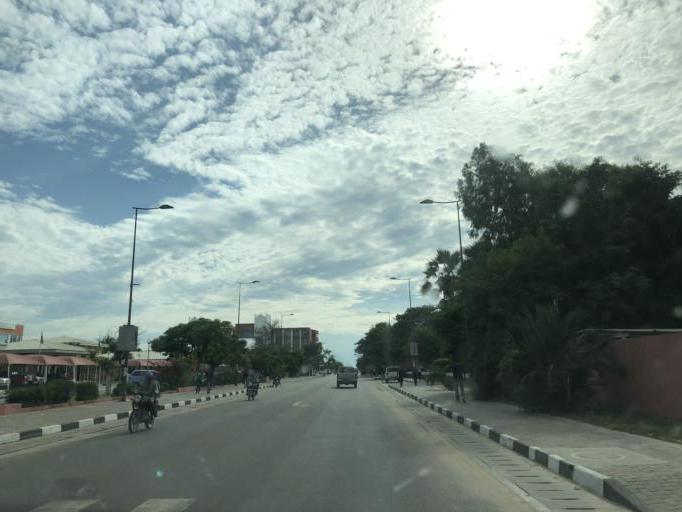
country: AO
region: Cunene
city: Ondjiva
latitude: -17.0676
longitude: 15.7248
